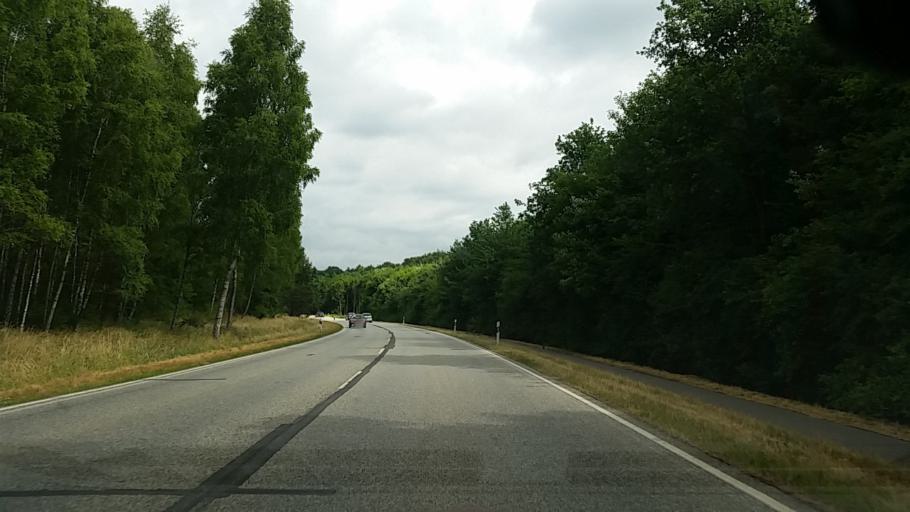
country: DE
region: Schleswig-Holstein
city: Kayhude
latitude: 53.7407
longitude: 10.1204
